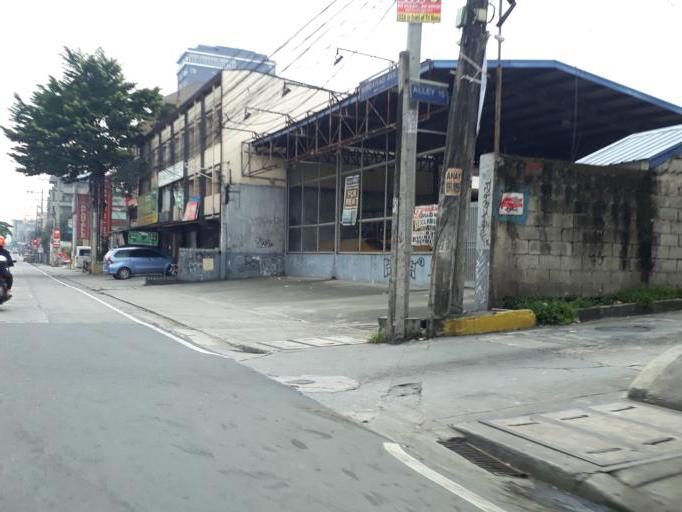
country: PH
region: Calabarzon
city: Bagong Pagasa
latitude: 14.6595
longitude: 121.0362
